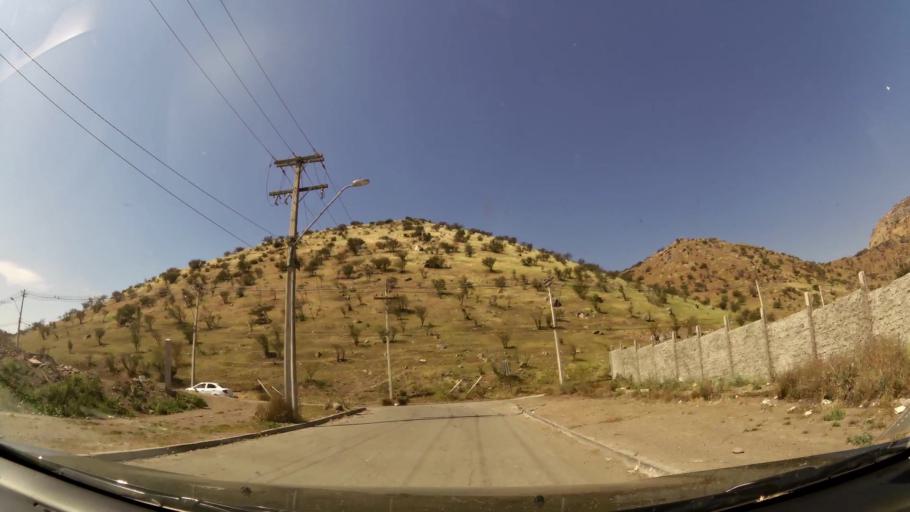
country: CL
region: Santiago Metropolitan
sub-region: Provincia de Santiago
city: Lo Prado
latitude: -33.3782
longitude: -70.7402
